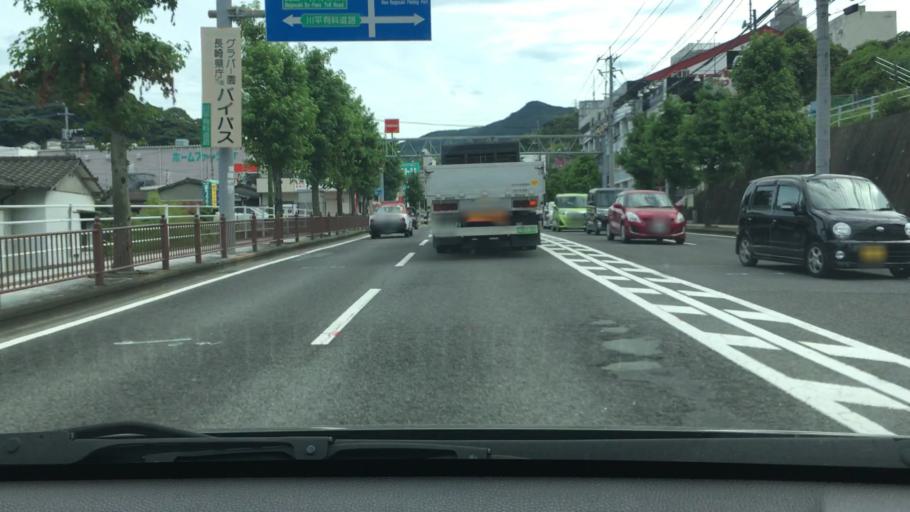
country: JP
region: Nagasaki
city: Togitsu
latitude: 32.8206
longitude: 129.8480
